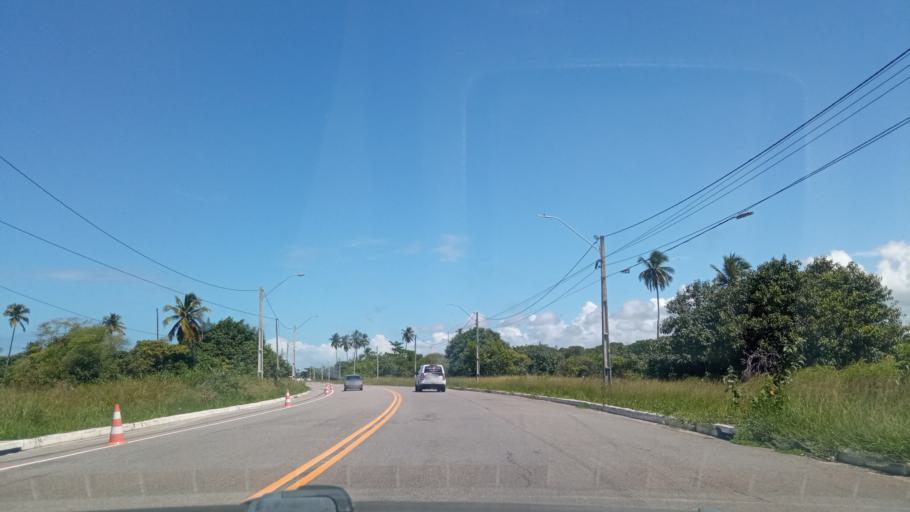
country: BR
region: Pernambuco
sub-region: Jaboatao Dos Guararapes
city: Jaboatao
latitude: -8.2332
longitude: -34.9368
